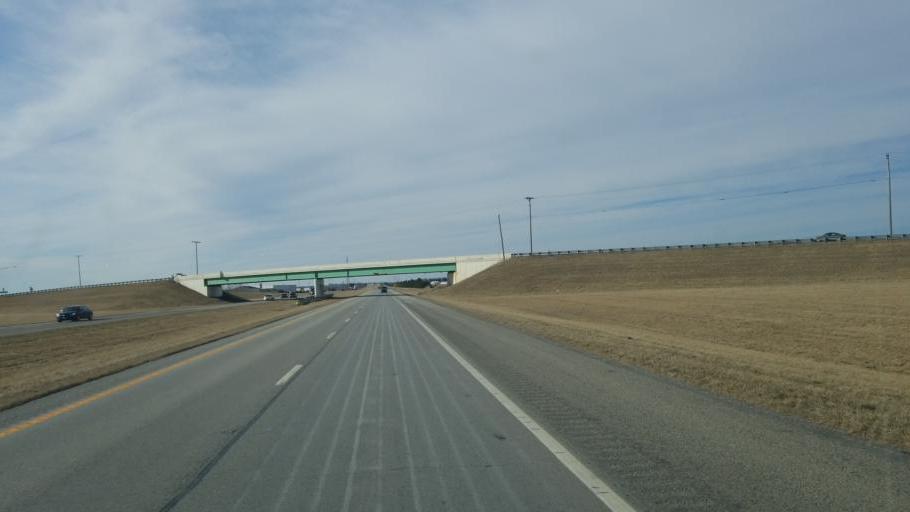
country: US
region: Ohio
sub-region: Allen County
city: Delphos
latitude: 40.8458
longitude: -84.3061
